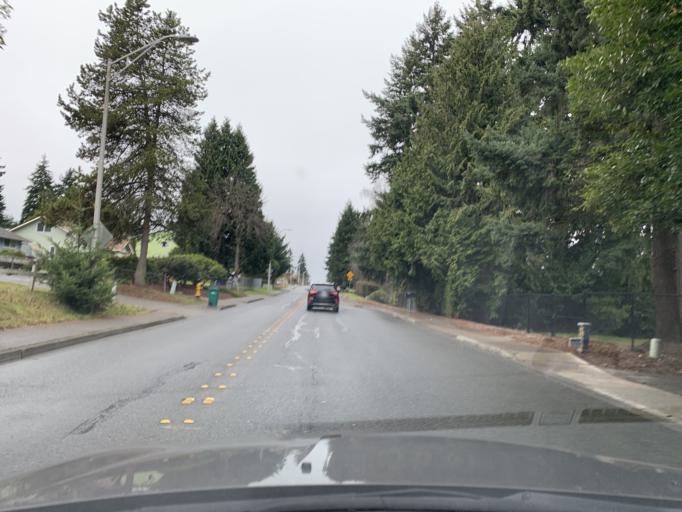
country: US
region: Washington
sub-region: King County
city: SeaTac
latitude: 47.4596
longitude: -122.2770
